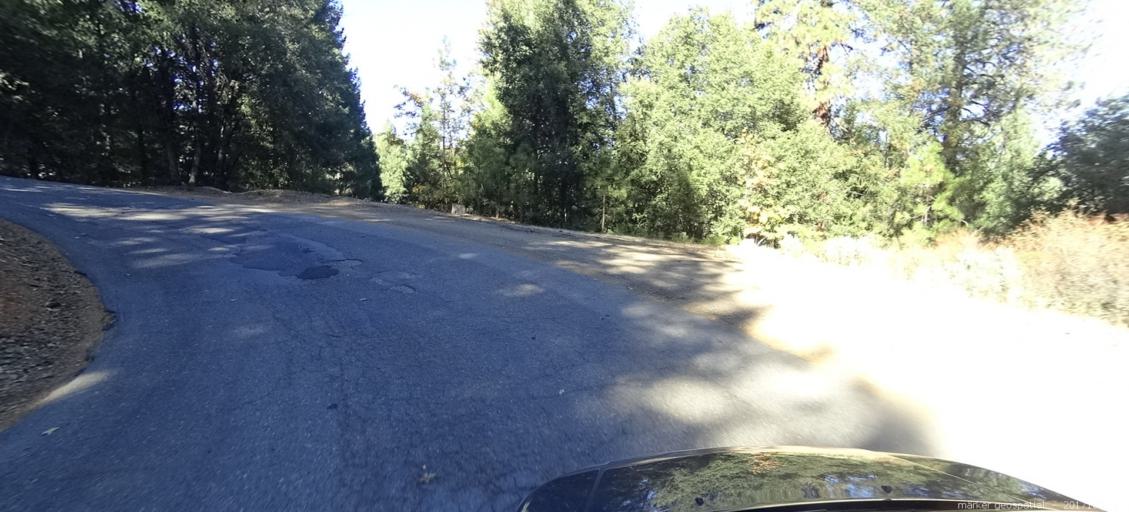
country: US
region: California
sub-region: Trinity County
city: Lewiston
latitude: 40.8157
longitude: -122.6393
